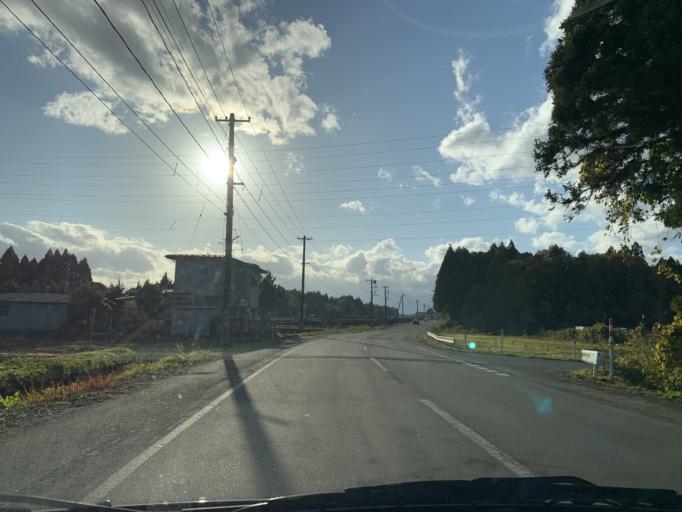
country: JP
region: Iwate
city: Mizusawa
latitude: 39.1150
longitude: 141.0867
